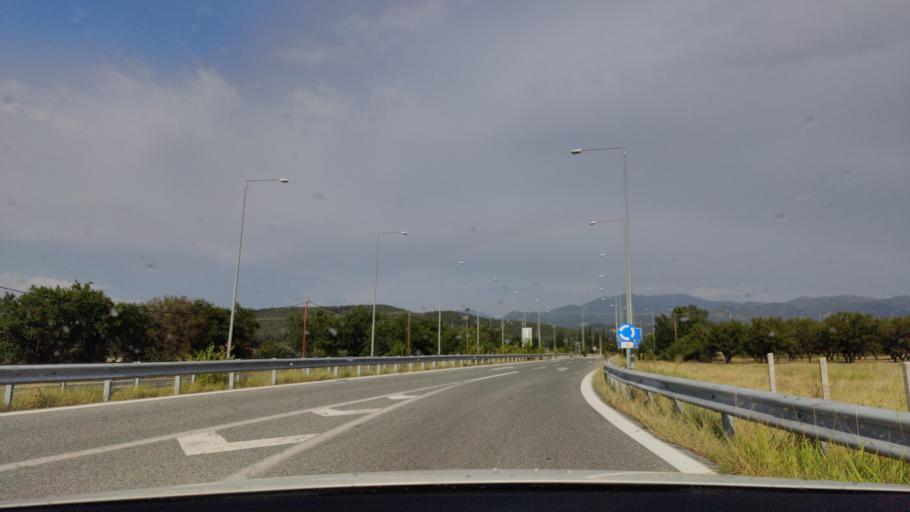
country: GR
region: Central Macedonia
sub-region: Nomos Serron
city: Sidirokastro
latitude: 41.2194
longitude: 23.3868
